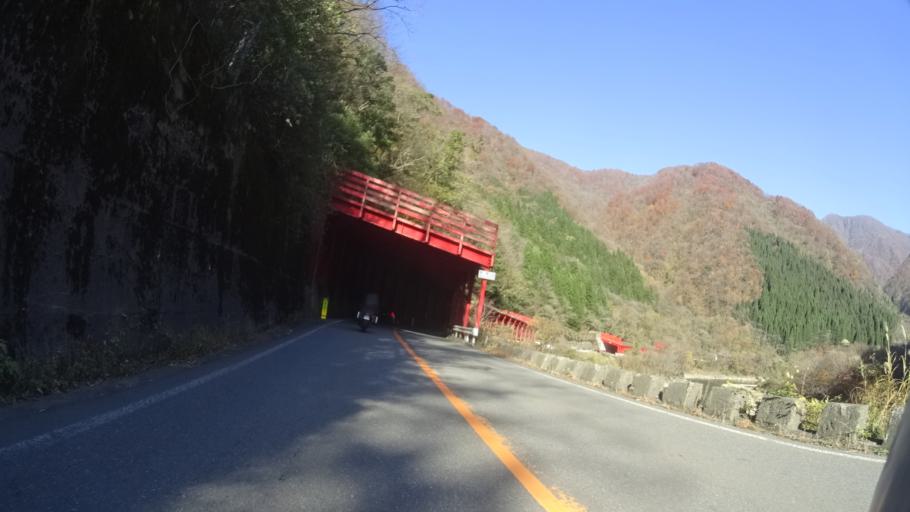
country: JP
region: Fukui
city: Ono
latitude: 35.9490
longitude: 136.6349
